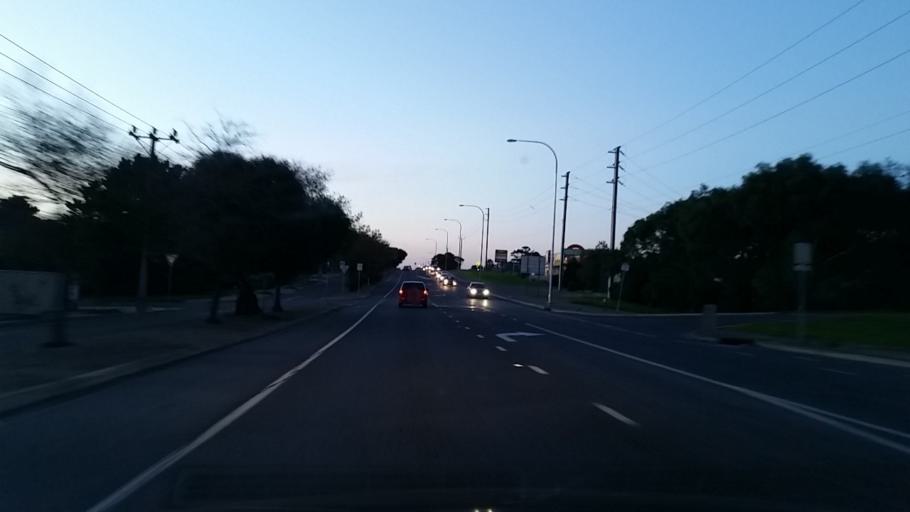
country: AU
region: South Australia
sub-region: Adelaide
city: Port Noarlunga
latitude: -35.1424
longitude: 138.4866
